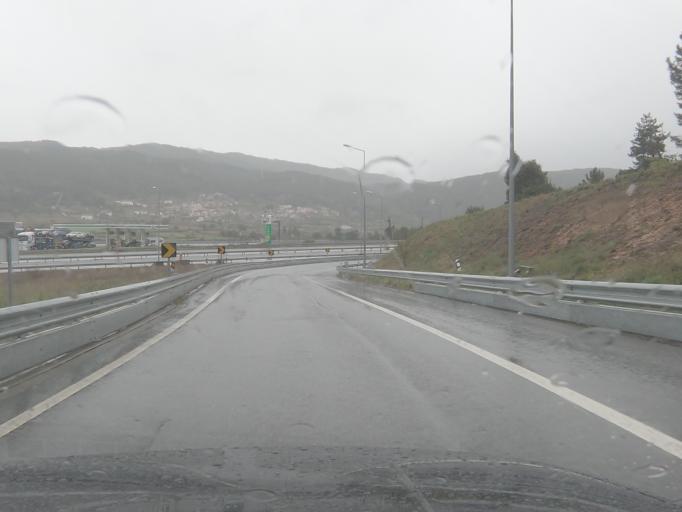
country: PT
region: Vila Real
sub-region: Boticas
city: Boticas
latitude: 41.6682
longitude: -7.5694
